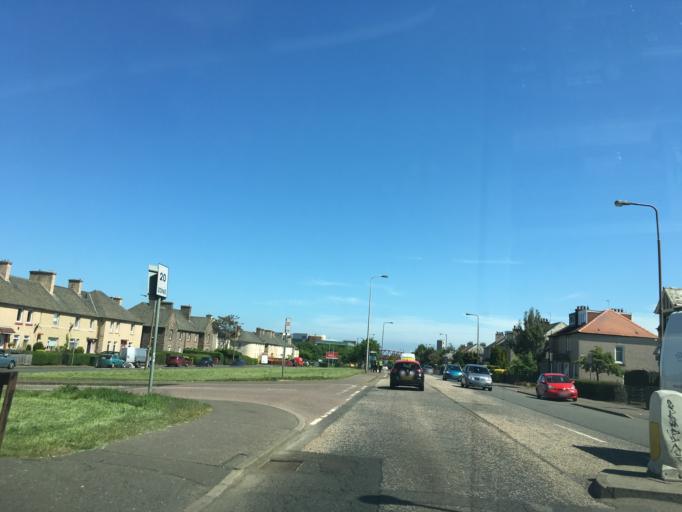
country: GB
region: Scotland
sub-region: Edinburgh
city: Edinburgh
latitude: 55.9676
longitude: -3.2446
